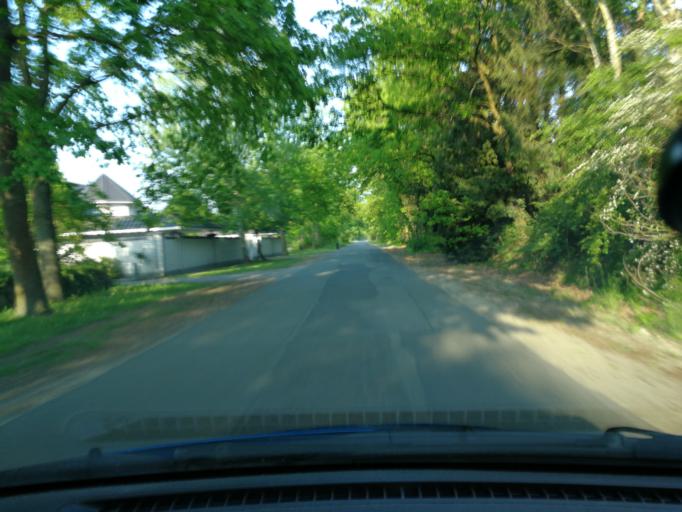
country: DE
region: Lower Saxony
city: Rullstorf
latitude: 53.2898
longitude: 10.5575
